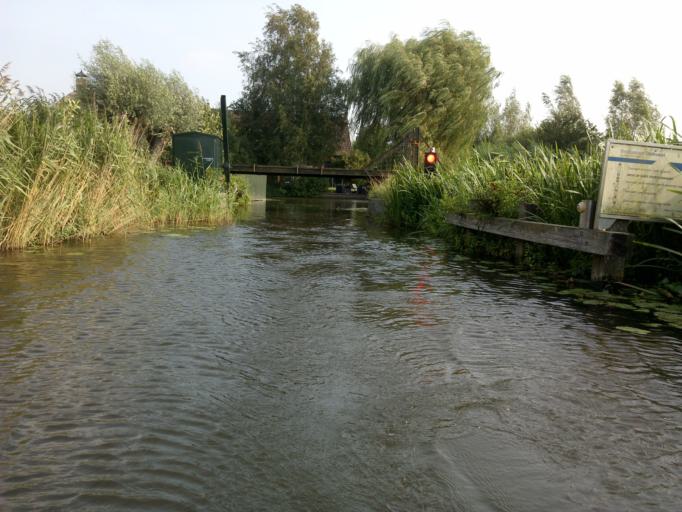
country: NL
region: South Holland
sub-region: Bodegraven-Reeuwijk
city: Bodegraven
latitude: 52.1098
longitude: 4.7560
